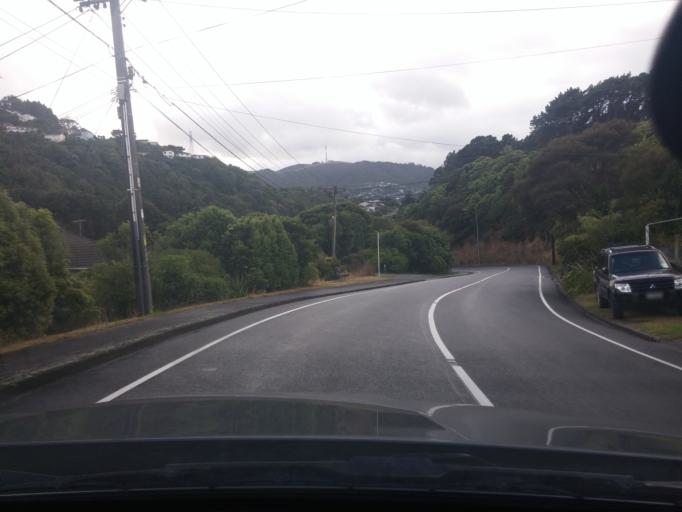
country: NZ
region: Wellington
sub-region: Wellington City
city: Kelburn
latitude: -41.2657
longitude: 174.7617
